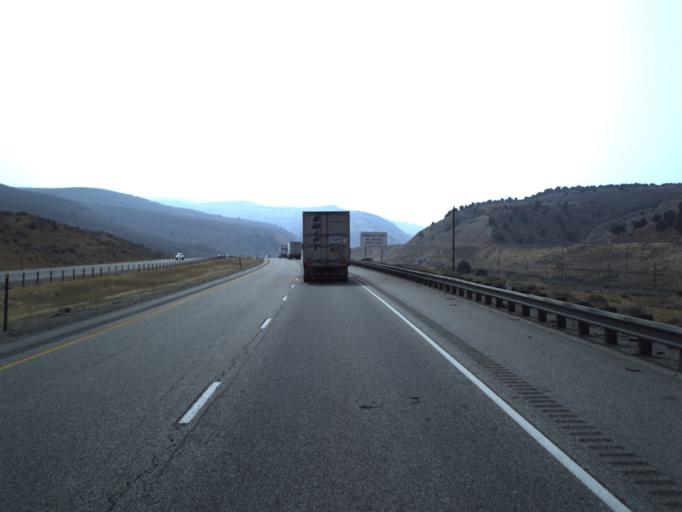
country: US
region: Utah
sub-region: Summit County
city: Coalville
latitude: 41.0979
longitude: -111.2176
